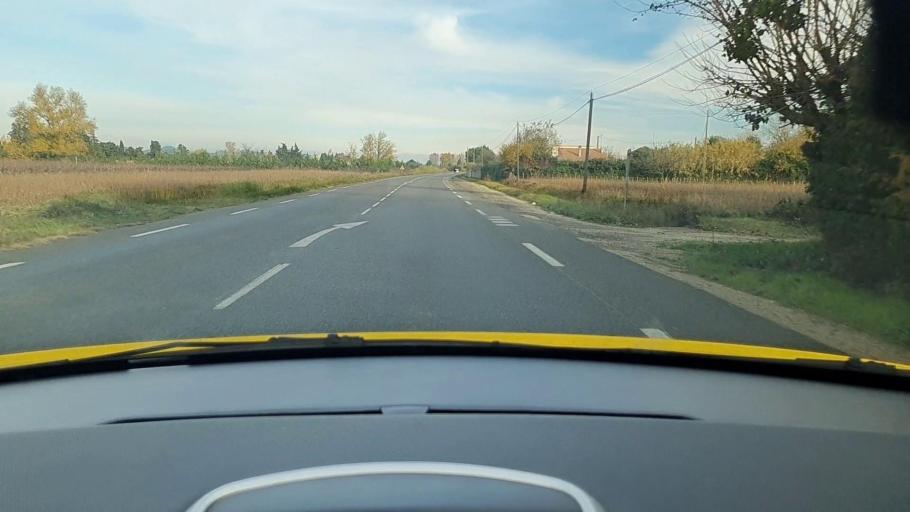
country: FR
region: Languedoc-Roussillon
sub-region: Departement du Gard
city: Beaucaire
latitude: 43.7693
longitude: 4.6202
